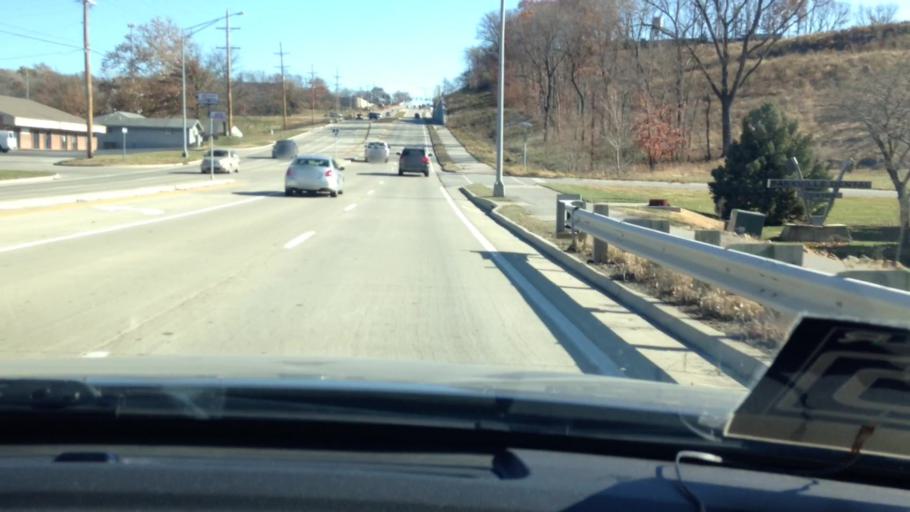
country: US
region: Missouri
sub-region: Platte County
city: Parkville
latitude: 39.2104
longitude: -94.6942
